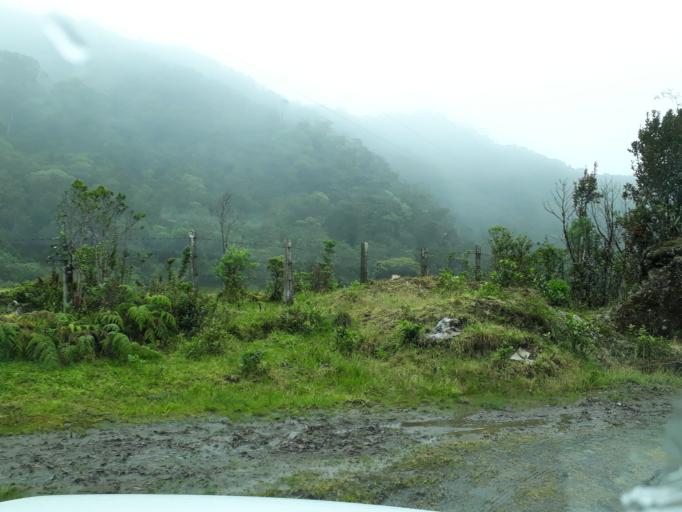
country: CO
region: Cundinamarca
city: Junin
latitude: 4.7127
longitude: -73.6288
